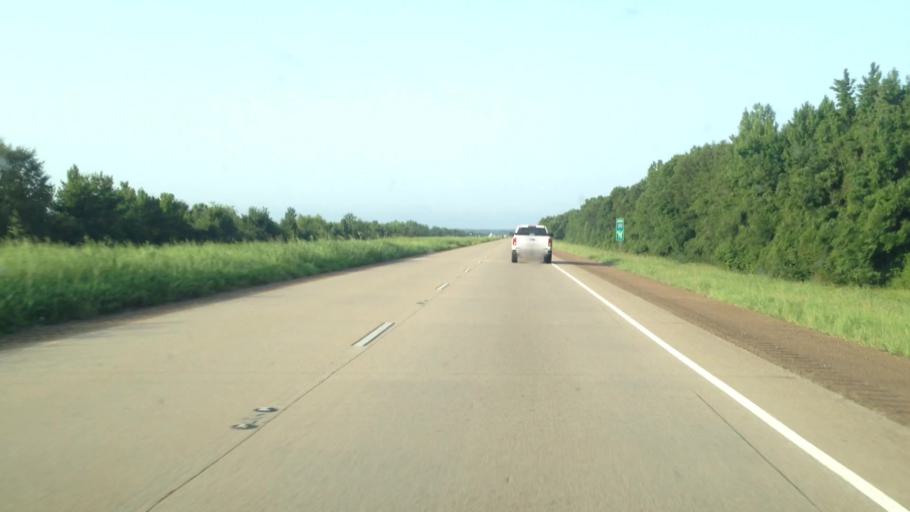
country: US
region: Louisiana
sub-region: Rapides Parish
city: Woodworth
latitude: 31.2258
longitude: -92.4661
